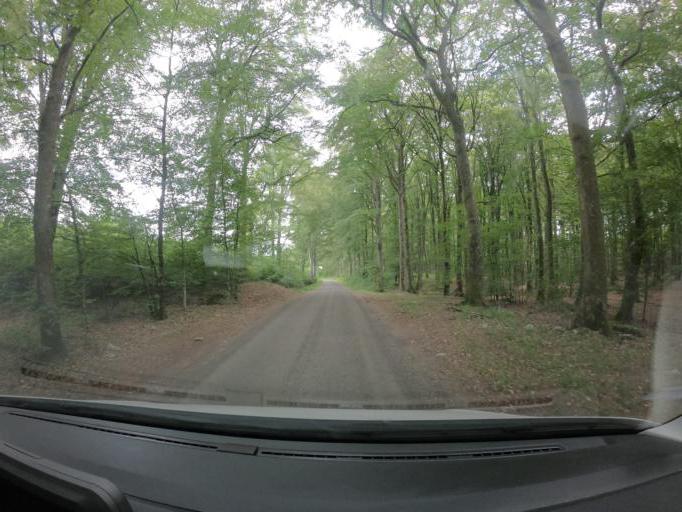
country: SE
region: Skane
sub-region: Hassleholms Kommun
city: Sosdala
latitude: 56.0690
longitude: 13.6676
